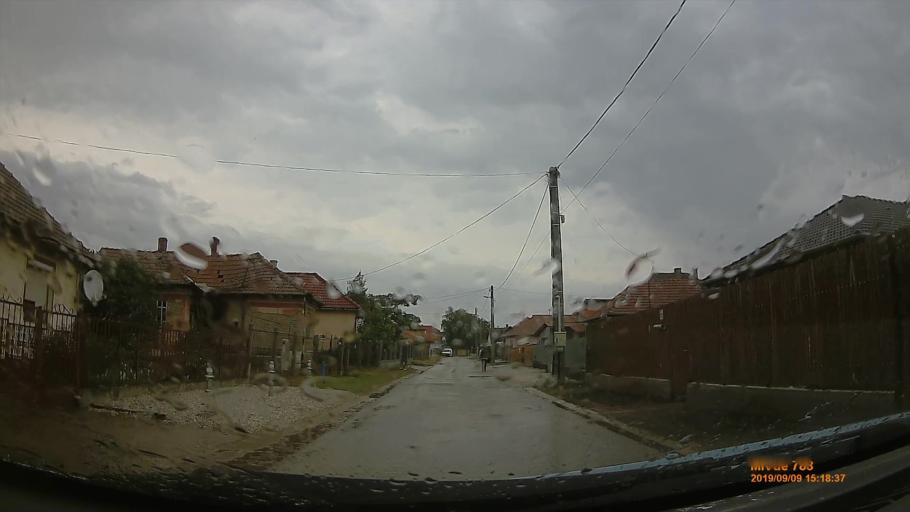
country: HU
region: Szabolcs-Szatmar-Bereg
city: Nyirpazony
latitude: 48.0143
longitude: 21.8290
